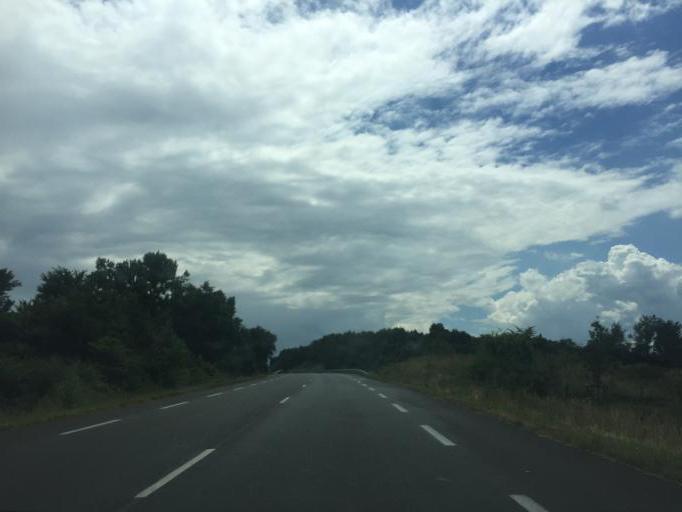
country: FR
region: Rhone-Alpes
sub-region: Departement de l'Isere
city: Janneyrias
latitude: 45.7862
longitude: 5.1318
